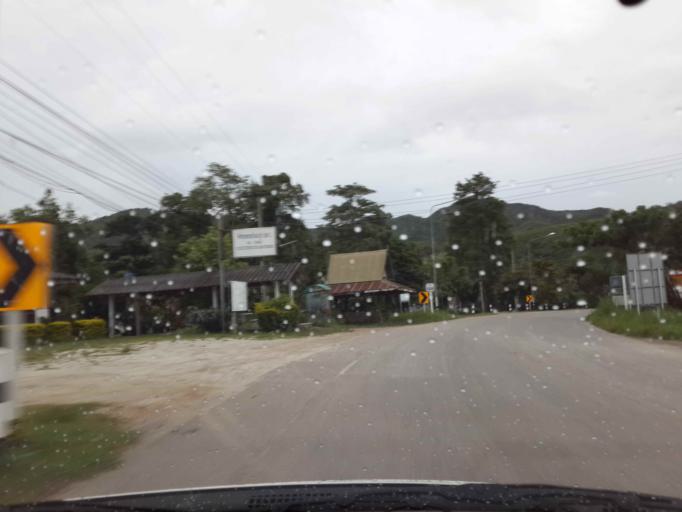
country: TH
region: Ratchaburi
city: Suan Phueng
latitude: 13.5866
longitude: 99.2460
